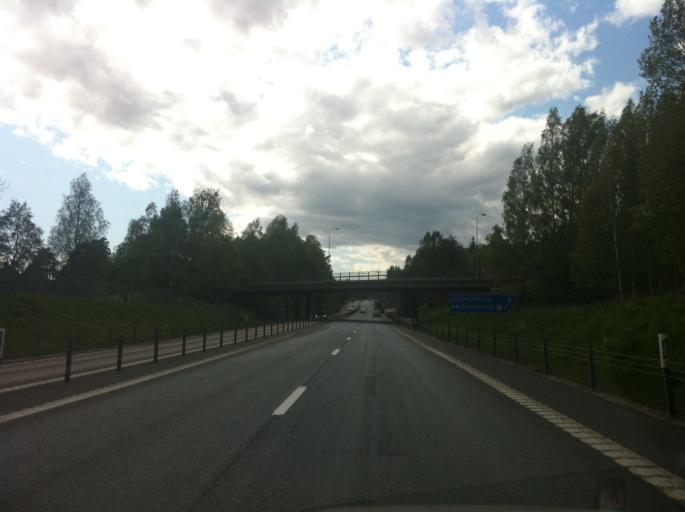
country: SE
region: Vaermland
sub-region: Kristinehamns Kommun
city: Kristinehamn
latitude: 59.3180
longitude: 14.1469
